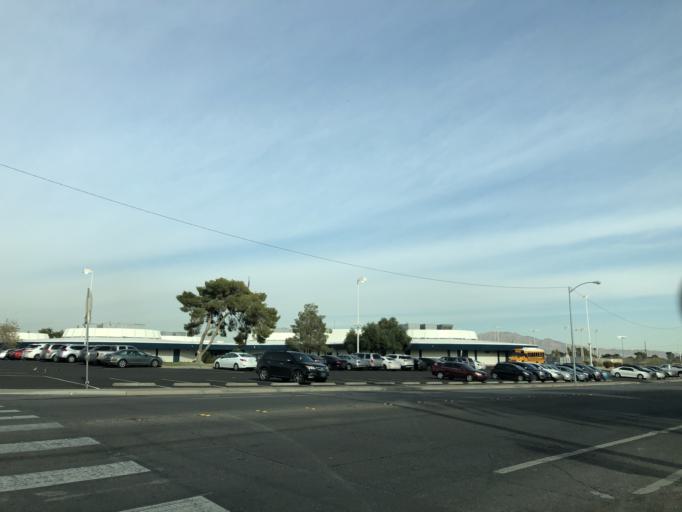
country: US
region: Nevada
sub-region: Clark County
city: Winchester
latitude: 36.1201
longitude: -115.1328
